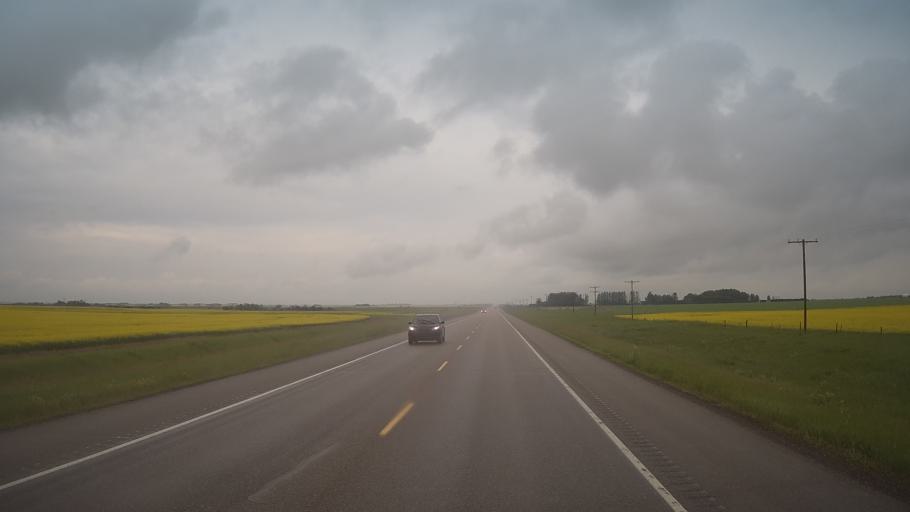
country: CA
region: Saskatchewan
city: Unity
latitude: 52.4349
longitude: -108.9622
